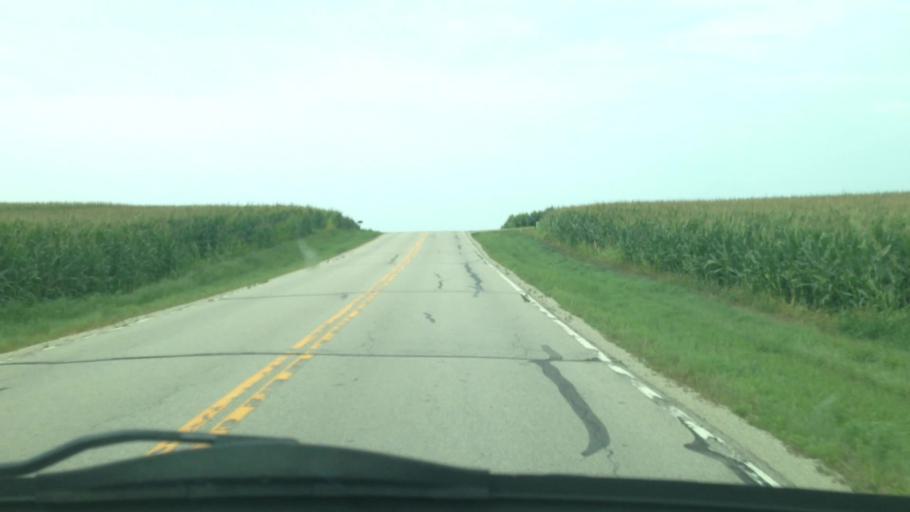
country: US
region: Minnesota
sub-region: Fillmore County
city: Preston
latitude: 43.7904
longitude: -91.9498
